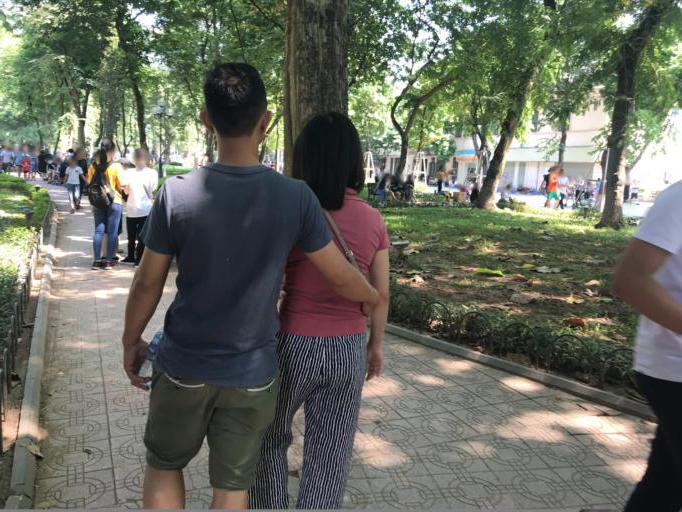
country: VN
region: Ha Noi
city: Hoan Kiem
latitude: 21.0293
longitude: 105.8536
